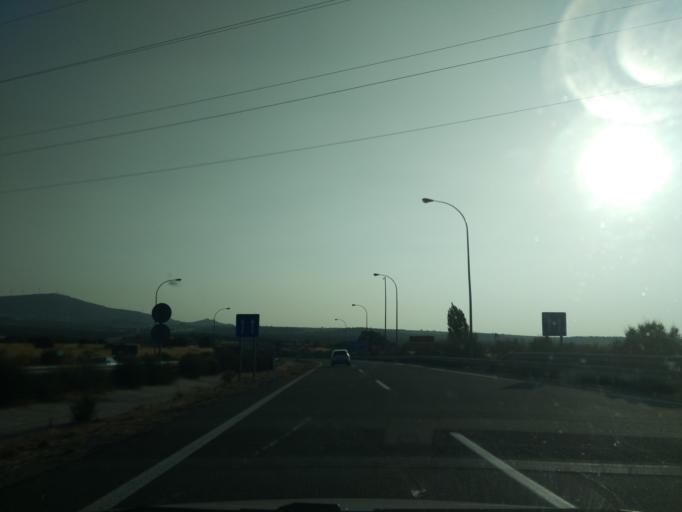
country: ES
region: Castille and Leon
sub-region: Provincia de Segovia
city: Villacastin
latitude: 40.7686
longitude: -4.4326
